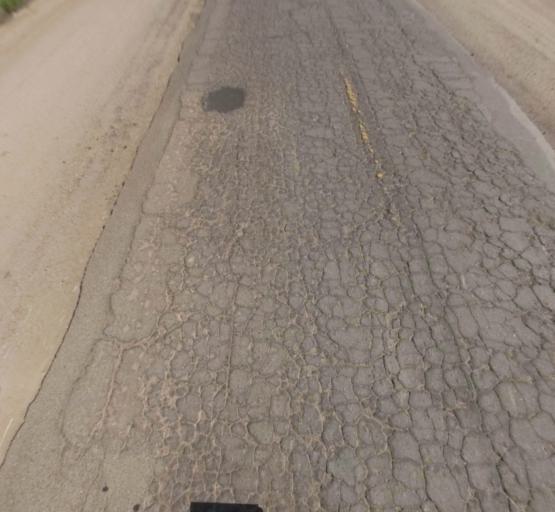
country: US
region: California
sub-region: Madera County
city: Chowchilla
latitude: 37.1370
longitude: -120.2927
